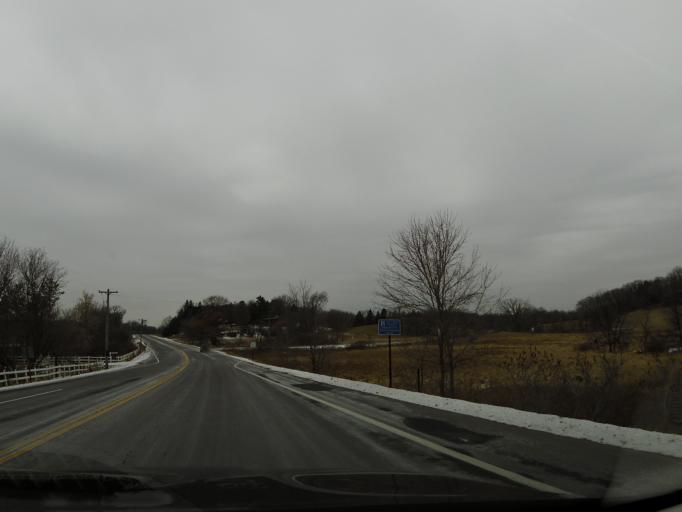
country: US
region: Minnesota
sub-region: Hennepin County
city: Medina
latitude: 45.0187
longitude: -93.5842
